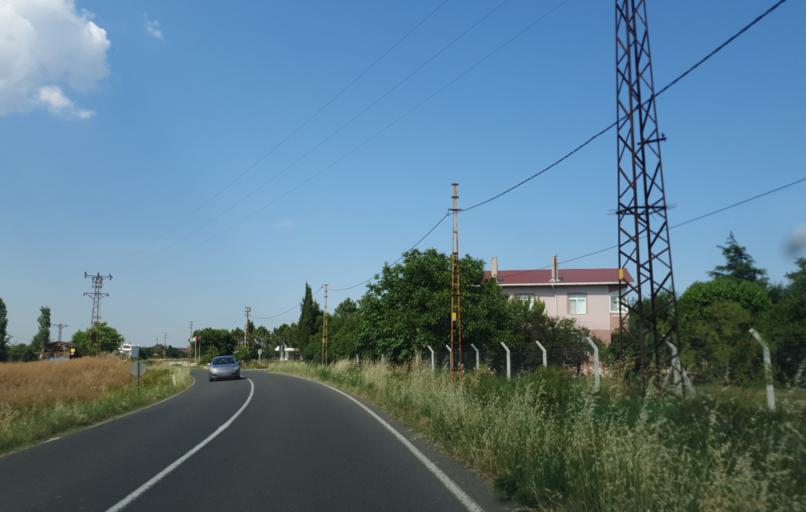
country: TR
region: Tekirdag
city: Muratli
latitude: 41.2131
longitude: 27.5395
